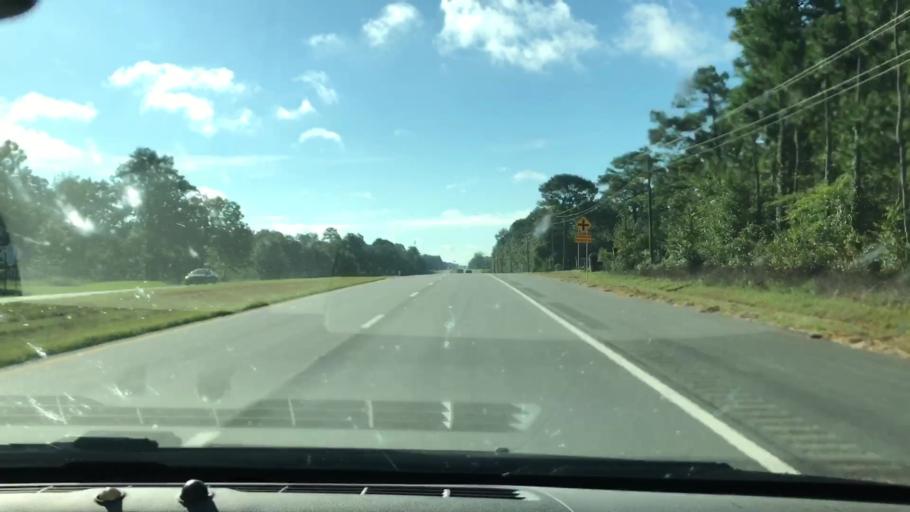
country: US
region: Georgia
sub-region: Lee County
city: Leesburg
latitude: 31.6701
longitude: -84.2876
